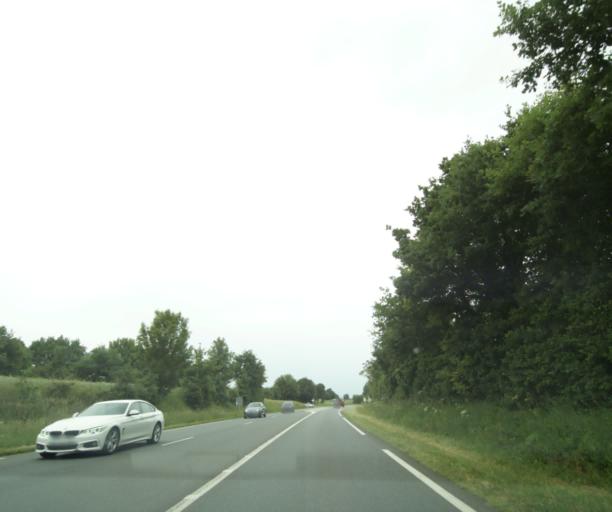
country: FR
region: Poitou-Charentes
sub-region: Departement des Deux-Sevres
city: Champdeniers-Saint-Denis
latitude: 46.4419
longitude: -0.3904
